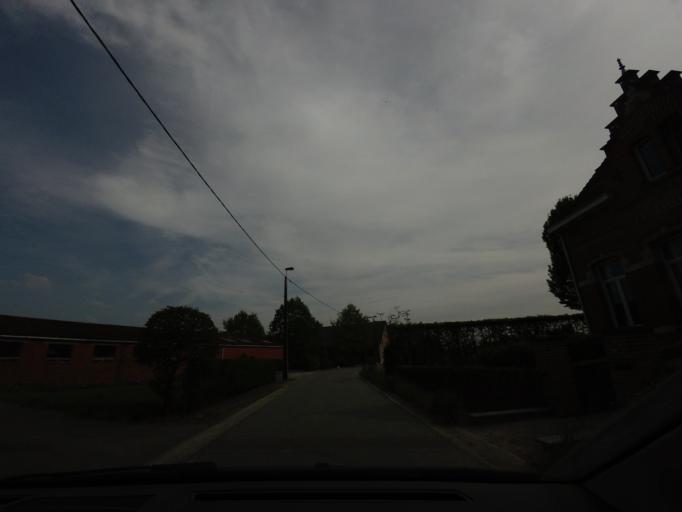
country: BE
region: Flanders
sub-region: Provincie Antwerpen
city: Lint
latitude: 51.1065
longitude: 4.4701
